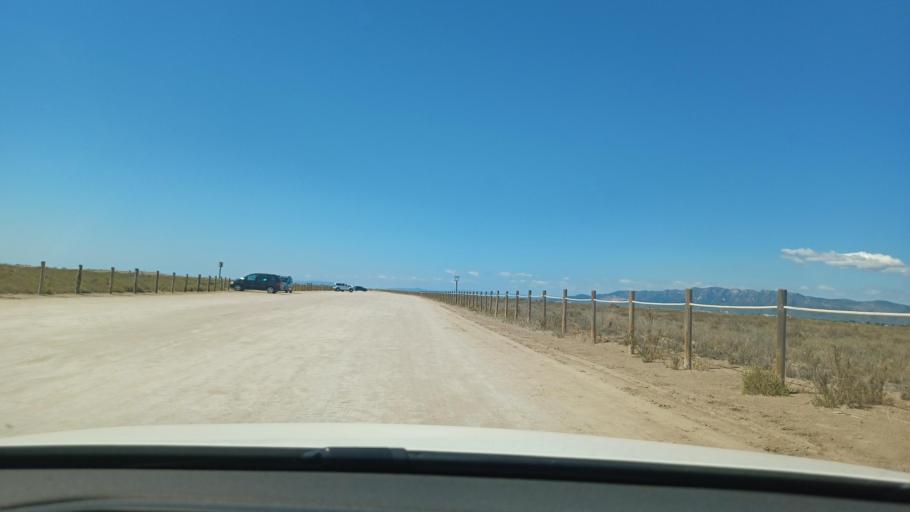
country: ES
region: Catalonia
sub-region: Provincia de Tarragona
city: Deltebre
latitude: 40.6458
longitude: 0.7624
